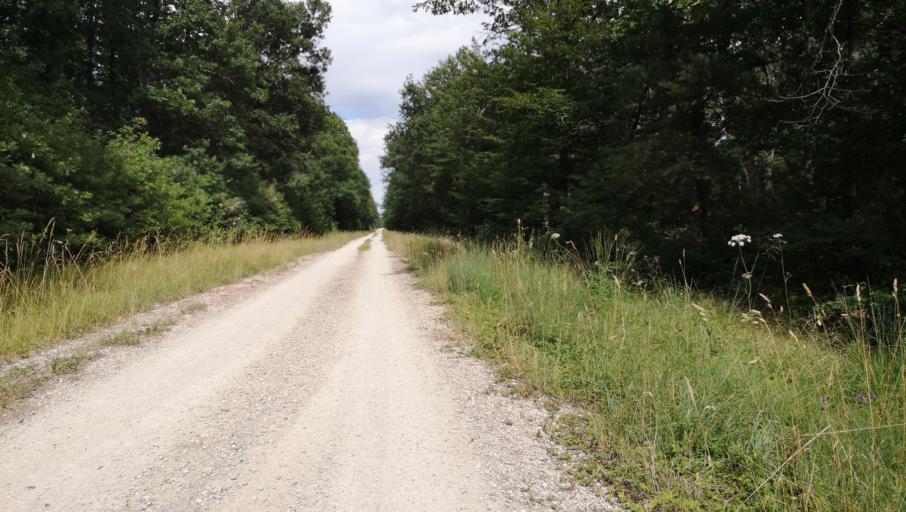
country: FR
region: Centre
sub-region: Departement du Loiret
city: Semoy
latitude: 47.9575
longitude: 1.9375
